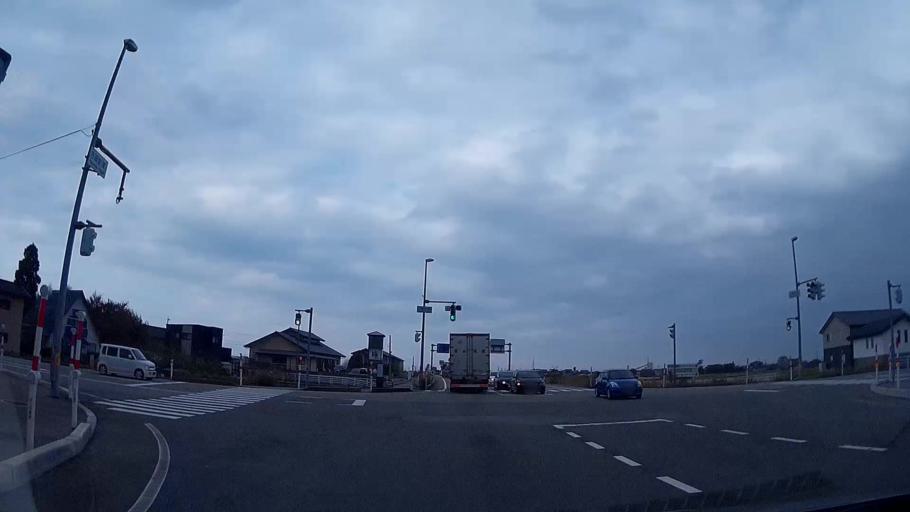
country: JP
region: Toyama
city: Nyuzen
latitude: 36.8919
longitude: 137.4443
